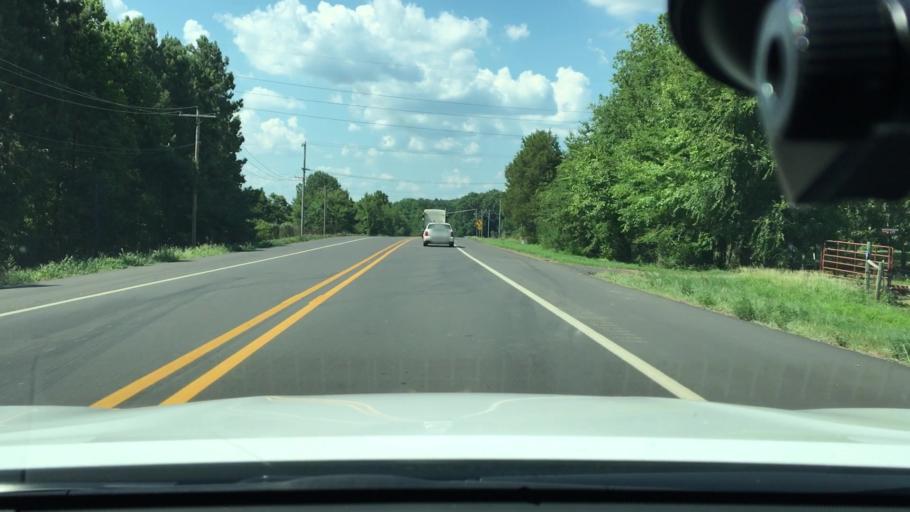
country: US
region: Arkansas
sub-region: Johnson County
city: Clarksville
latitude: 35.4476
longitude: -93.5291
